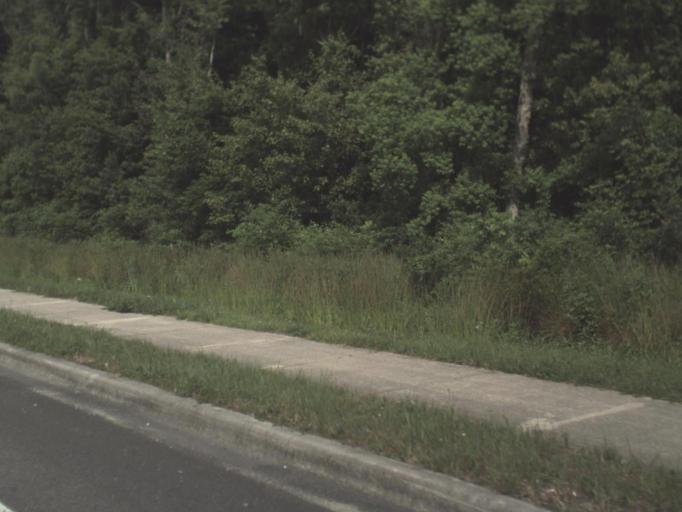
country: US
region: Florida
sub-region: Saint Johns County
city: Saint Augustine South
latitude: 29.8209
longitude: -81.3829
